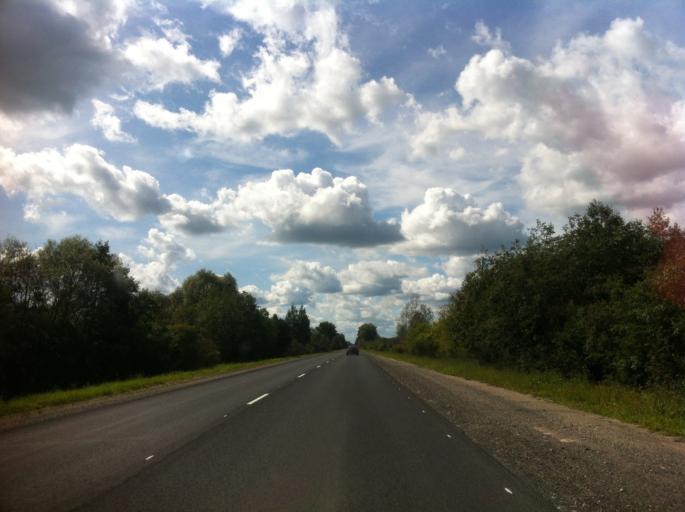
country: RU
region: Pskov
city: Izborsk
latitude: 57.7373
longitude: 27.9985
